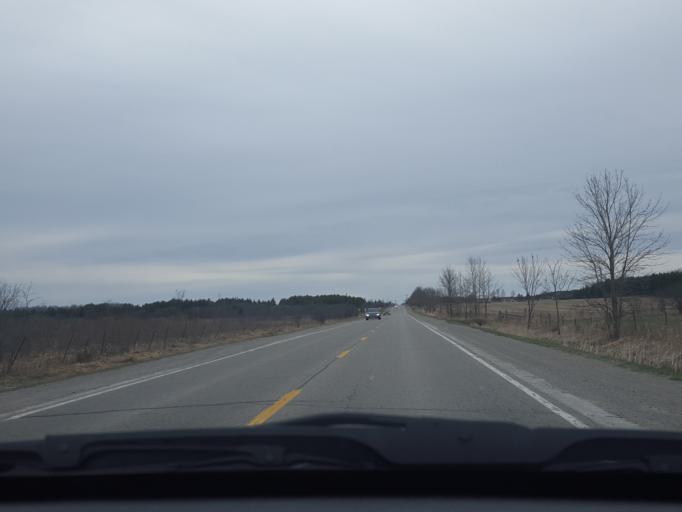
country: CA
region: Ontario
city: Uxbridge
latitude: 44.3073
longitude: -79.1756
